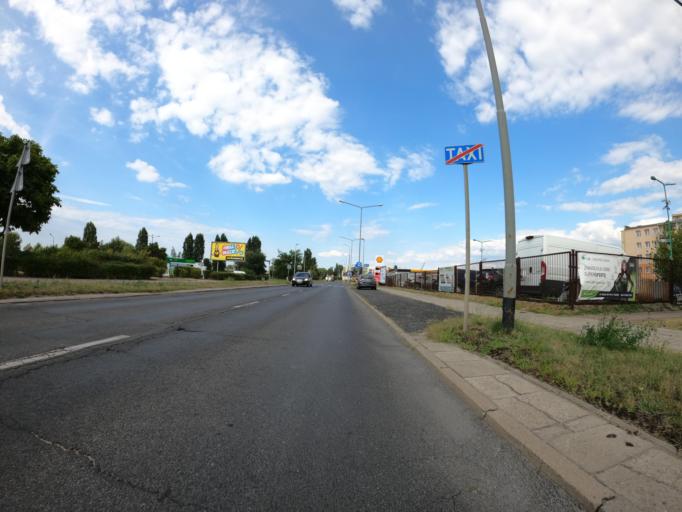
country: PL
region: West Pomeranian Voivodeship
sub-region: Szczecin
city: Szczecin
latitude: 53.3796
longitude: 14.6505
